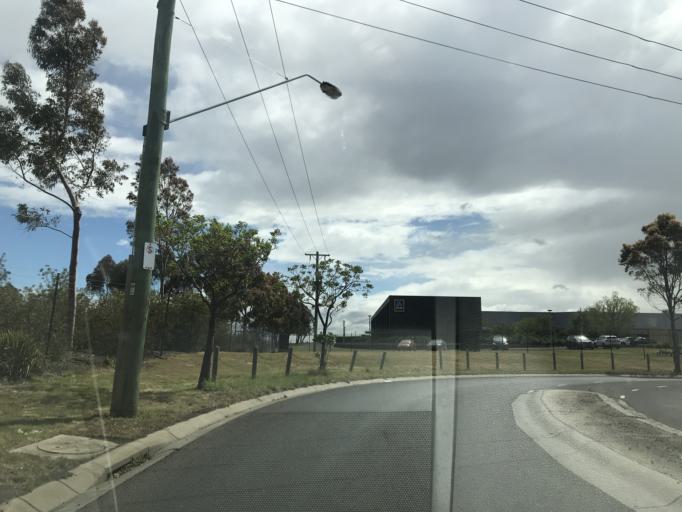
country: AU
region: Victoria
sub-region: Brimbank
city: Derrimut
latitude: -37.8050
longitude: 144.7796
